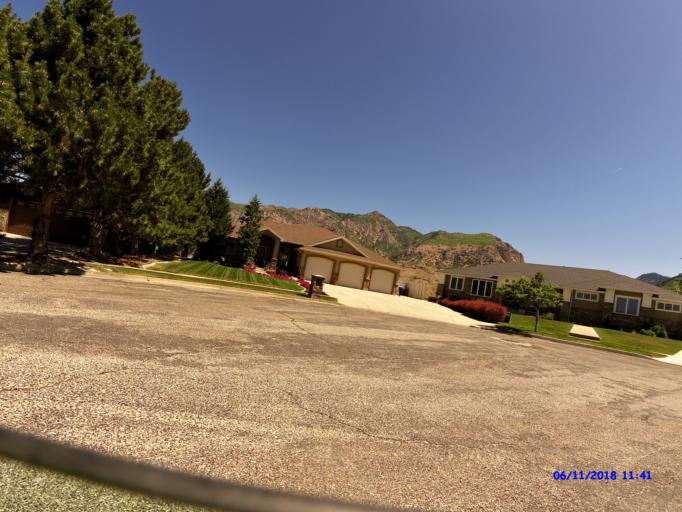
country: US
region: Utah
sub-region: Weber County
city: Ogden
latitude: 41.2308
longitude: -111.9432
